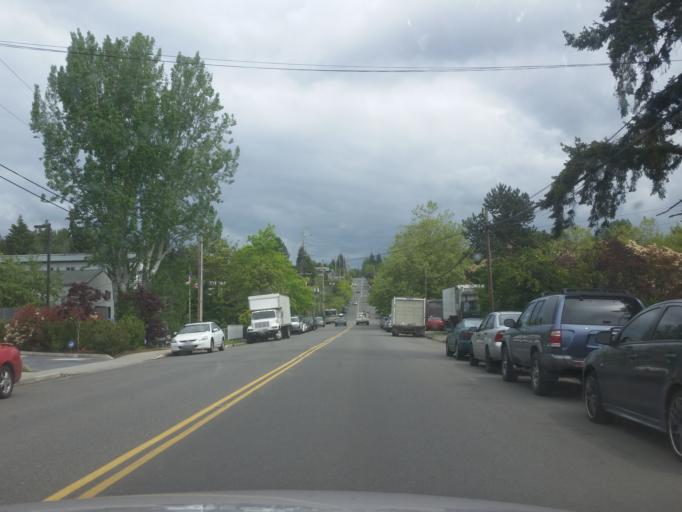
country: US
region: Washington
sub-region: King County
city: Kirkland
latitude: 47.6806
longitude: -122.1963
